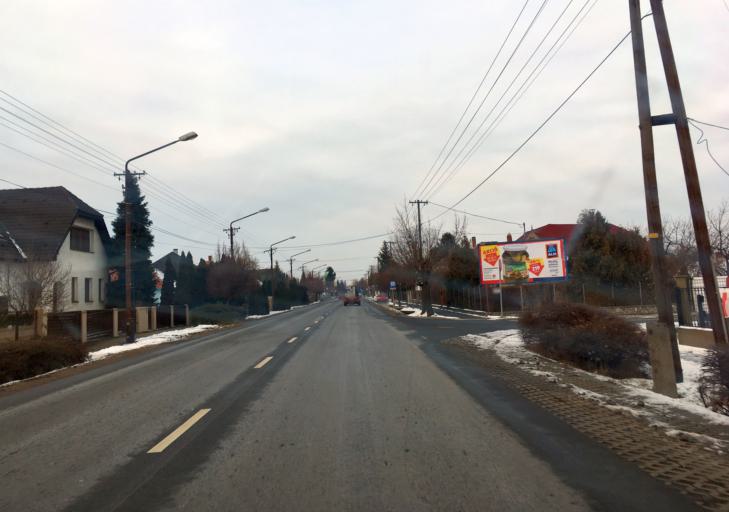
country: HU
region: Gyor-Moson-Sopron
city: Mosonmagyarovar
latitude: 47.8636
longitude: 17.2674
